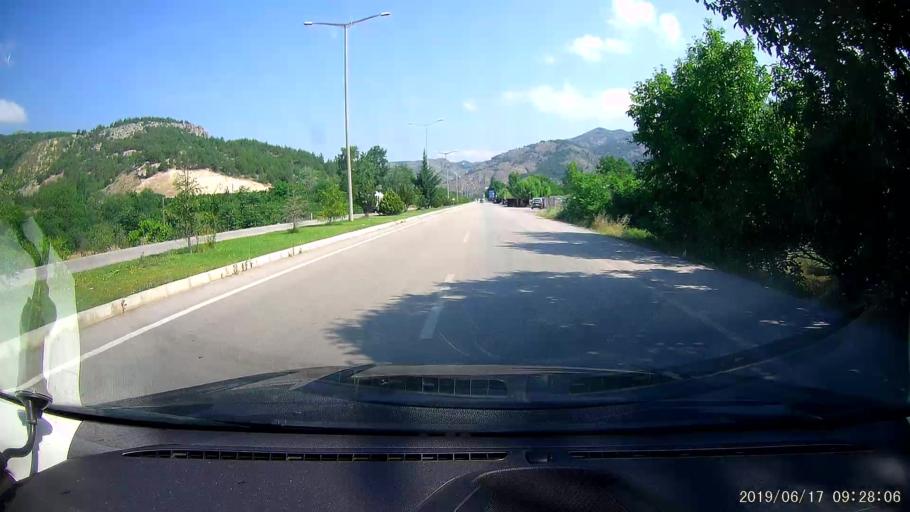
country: TR
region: Amasya
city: Amasya
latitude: 40.6846
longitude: 35.8232
